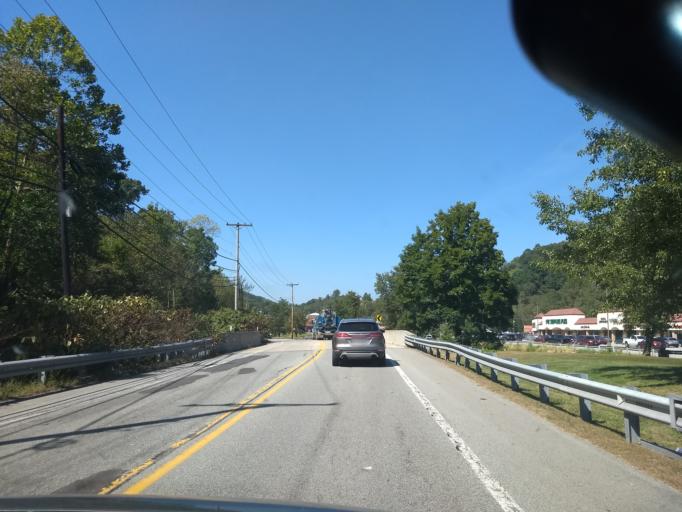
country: US
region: Pennsylvania
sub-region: Allegheny County
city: White Oak
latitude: 40.3352
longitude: -79.8049
